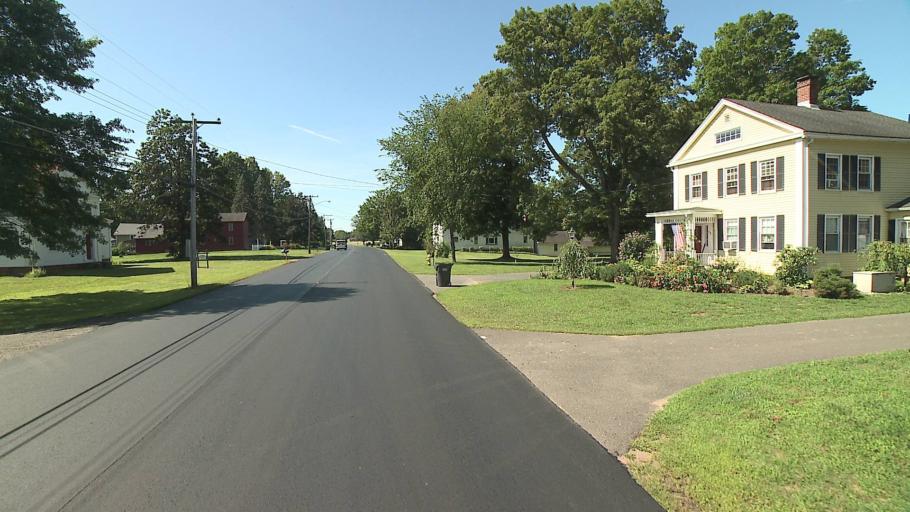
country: US
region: Connecticut
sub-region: Hartford County
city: Suffield Depot
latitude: 41.9900
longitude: -72.7030
